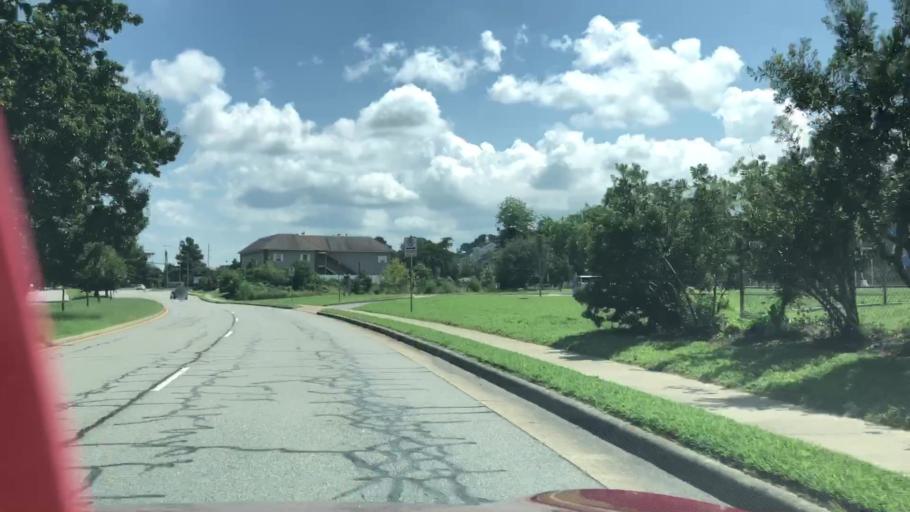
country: US
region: Virginia
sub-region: City of Virginia Beach
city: Virginia Beach
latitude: 36.8696
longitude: -76.0341
